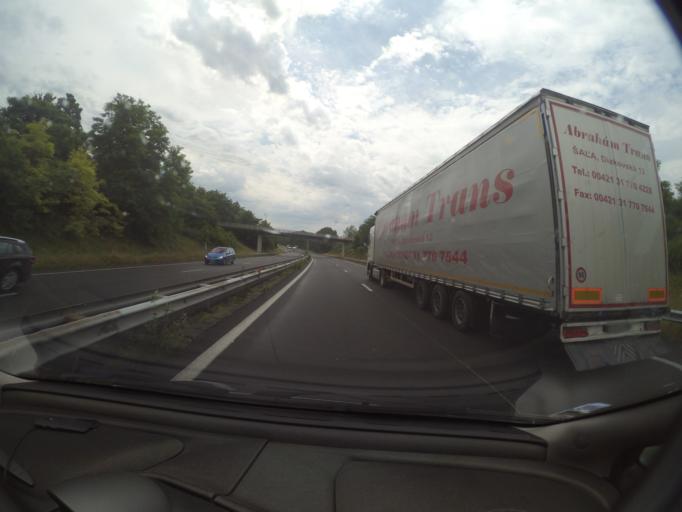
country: FR
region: Pays de la Loire
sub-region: Departement de Maine-et-Loire
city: Seiches-sur-le-Loir
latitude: 47.5812
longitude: -0.3332
